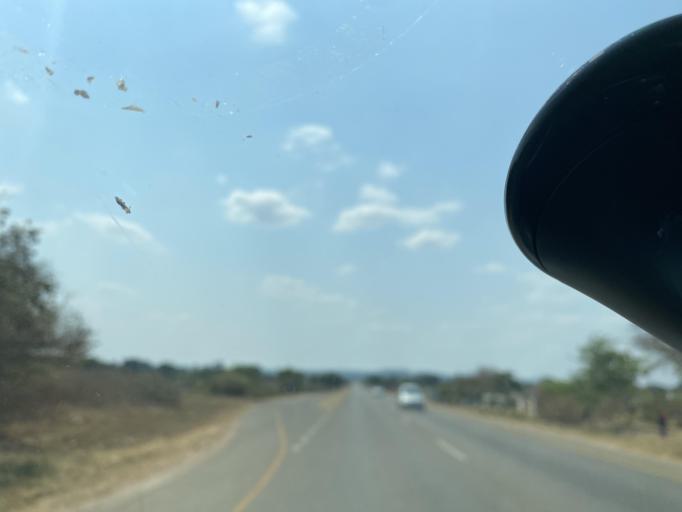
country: ZM
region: Lusaka
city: Chongwe
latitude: -15.5650
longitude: 28.6902
